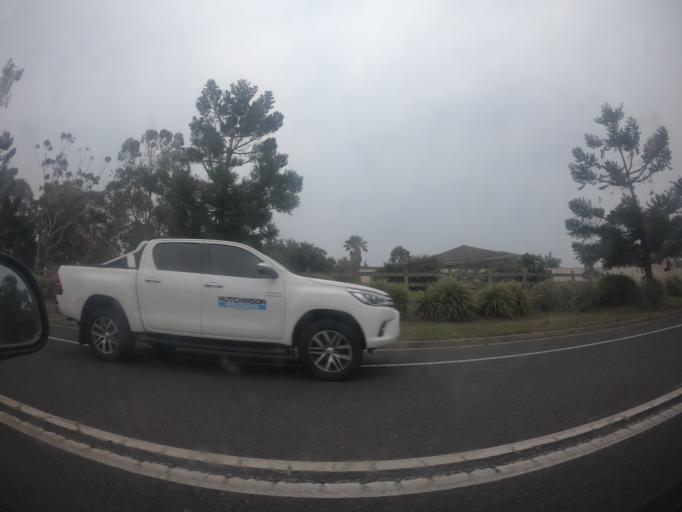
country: AU
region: New South Wales
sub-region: Shellharbour
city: Croom
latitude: -34.5740
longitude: 150.8326
